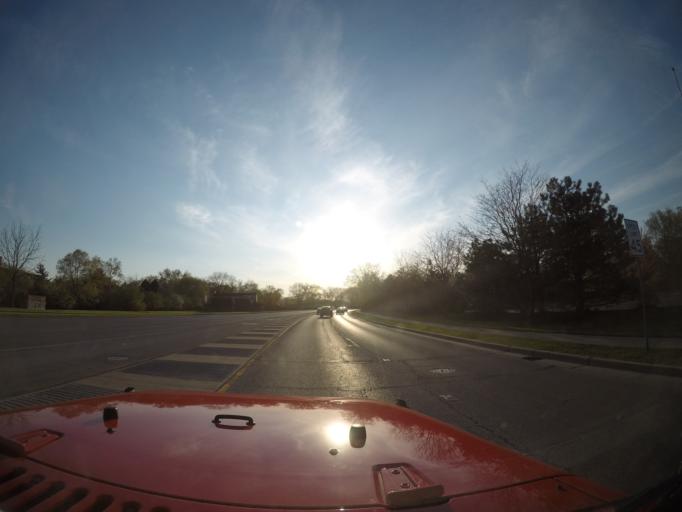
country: US
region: Illinois
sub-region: Cook County
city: Northbrook
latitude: 42.0787
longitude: -87.8405
